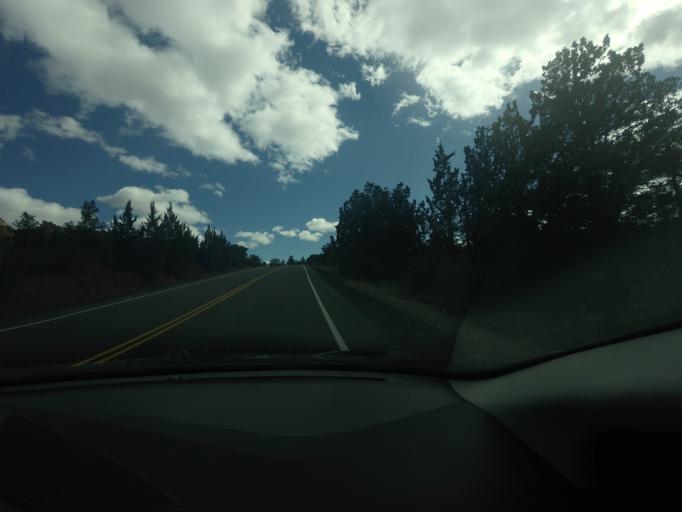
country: US
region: Arizona
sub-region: Yavapai County
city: West Sedona
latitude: 34.8940
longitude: -111.8252
